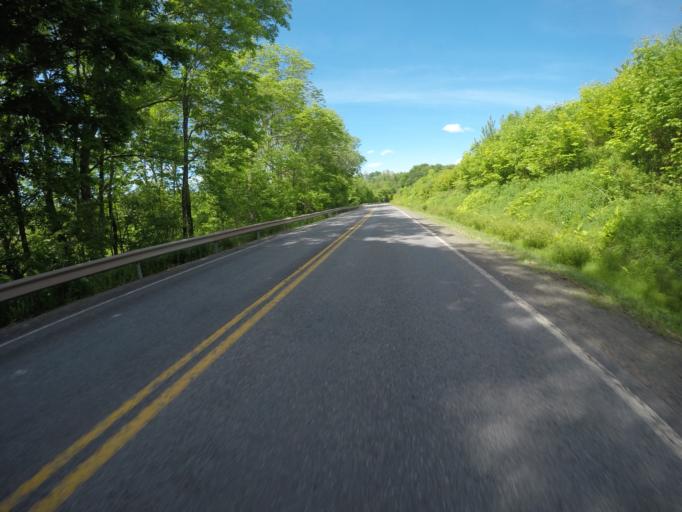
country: US
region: New York
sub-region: Delaware County
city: Delhi
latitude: 42.1576
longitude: -74.7979
